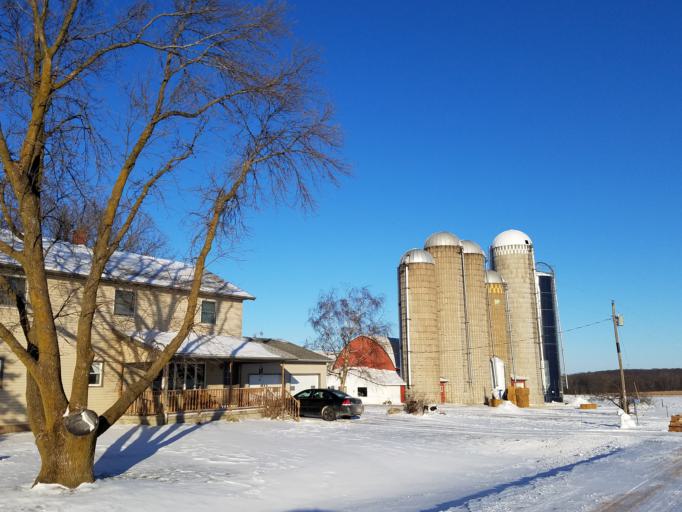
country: US
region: Wisconsin
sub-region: Clark County
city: Loyal
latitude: 44.6149
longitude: -90.4271
